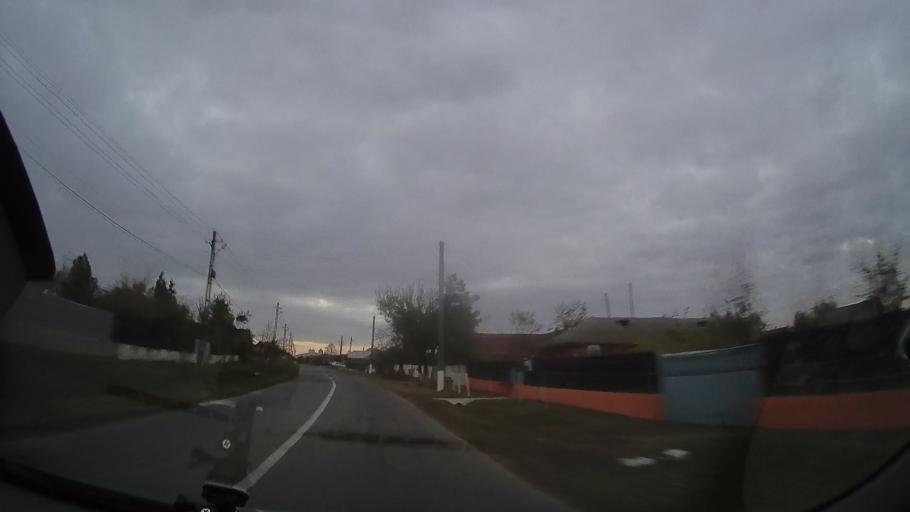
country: RO
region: Tulcea
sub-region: Comuna Mihai Bravu
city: Turda
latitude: 44.9720
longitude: 28.6270
